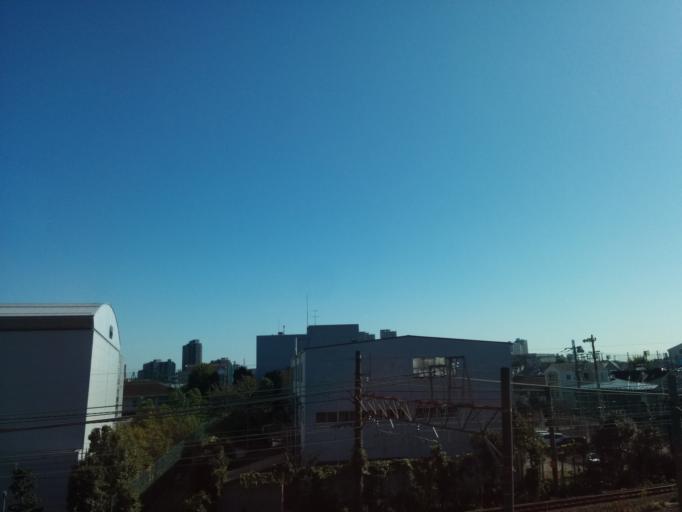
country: JP
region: Kanagawa
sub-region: Kawasaki-shi
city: Kawasaki
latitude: 35.5699
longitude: 139.6645
